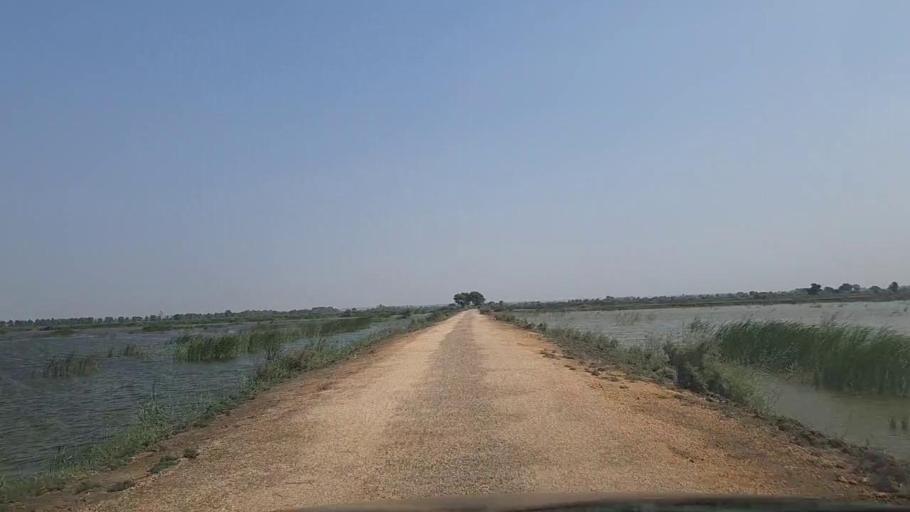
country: PK
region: Sindh
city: Mirpur Sakro
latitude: 24.6229
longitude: 67.7904
